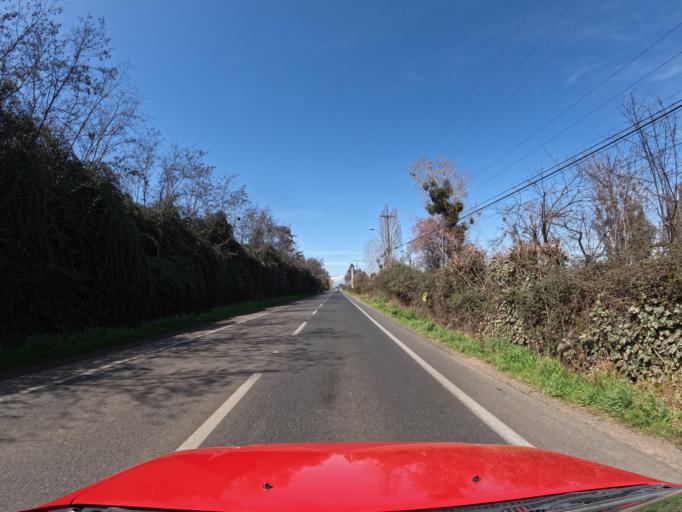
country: CL
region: Maule
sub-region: Provincia de Curico
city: Teno
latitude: -34.9640
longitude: -71.0628
